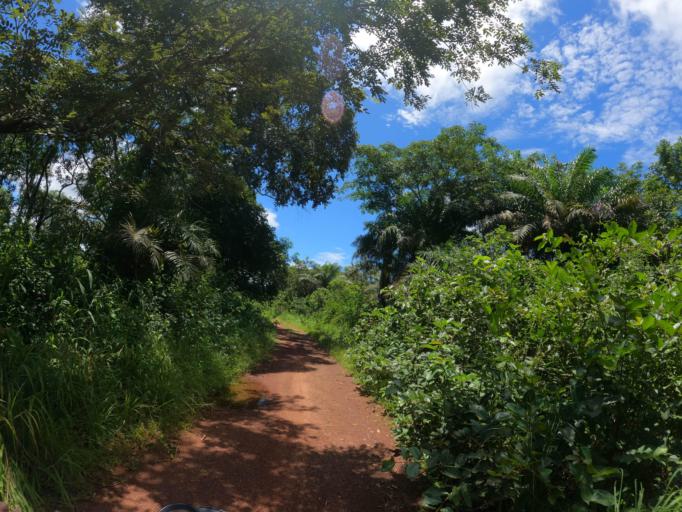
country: SL
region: Northern Province
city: Makeni
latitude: 9.0827
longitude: -12.2693
